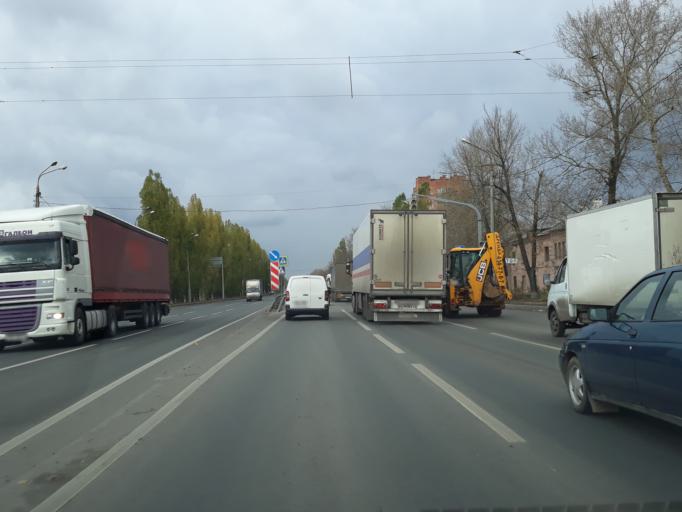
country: RU
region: Nizjnij Novgorod
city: Nizhniy Novgorod
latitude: 56.2713
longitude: 43.9102
